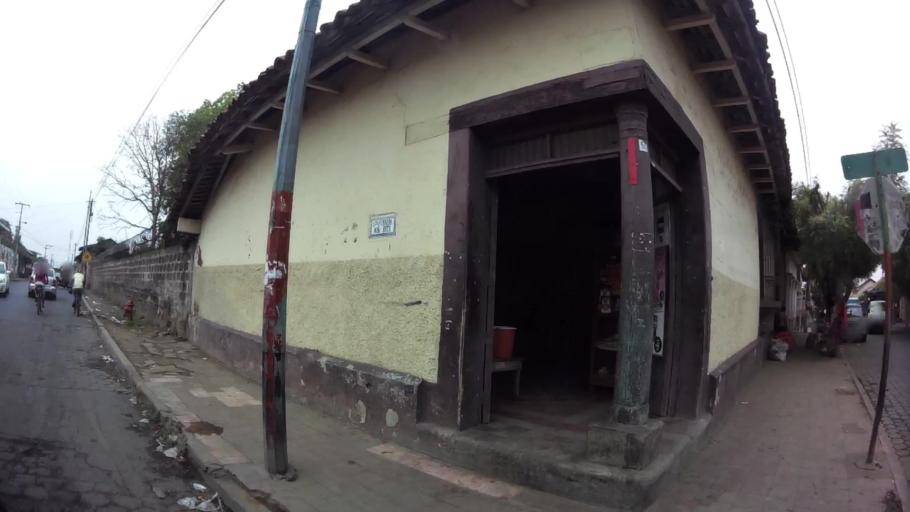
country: NI
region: Leon
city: Leon
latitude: 12.4400
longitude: -86.8718
